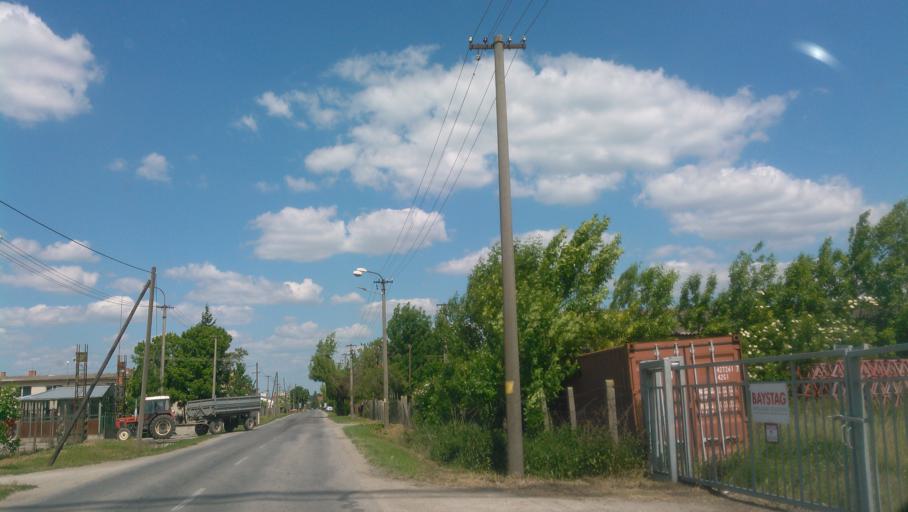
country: SK
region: Nitriansky
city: Kolarovo
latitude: 47.9071
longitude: 17.9805
